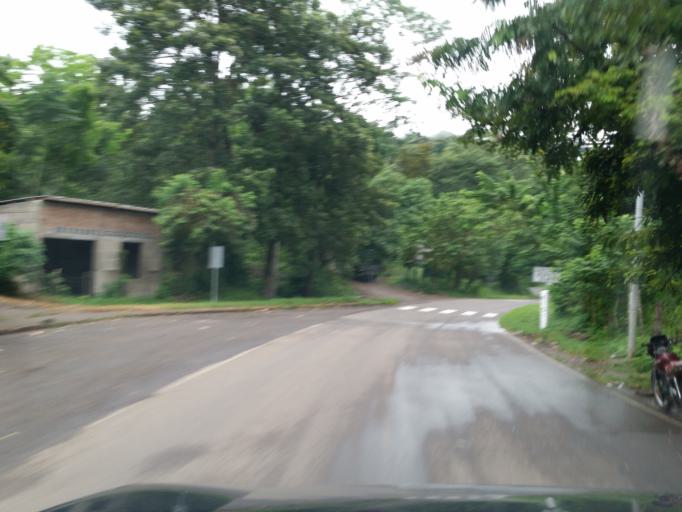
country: NI
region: Matagalpa
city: San Ramon
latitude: 13.0062
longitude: -85.8071
